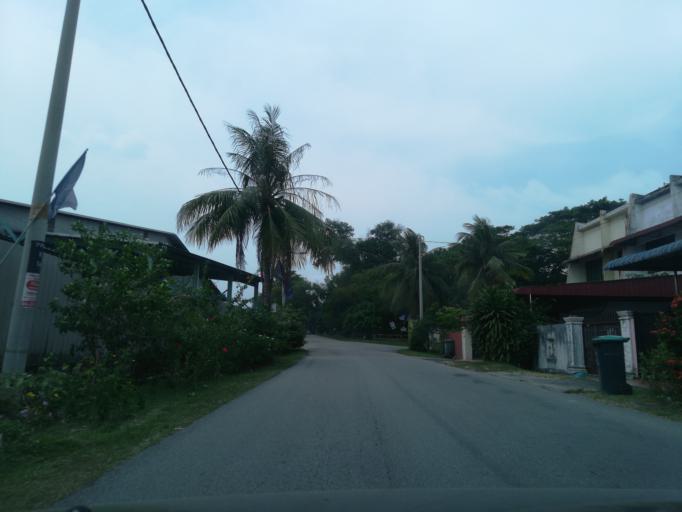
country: MY
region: Kedah
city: Kulim
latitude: 5.4015
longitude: 100.5618
